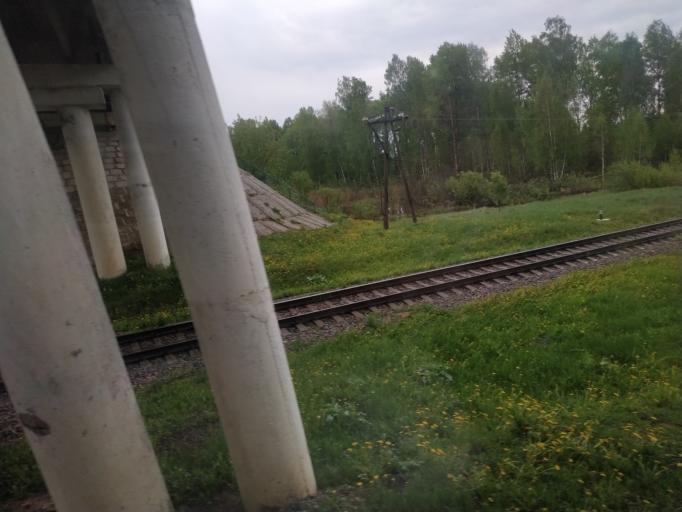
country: RU
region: Kaluga
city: Baryatino
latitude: 54.3516
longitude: 34.3308
